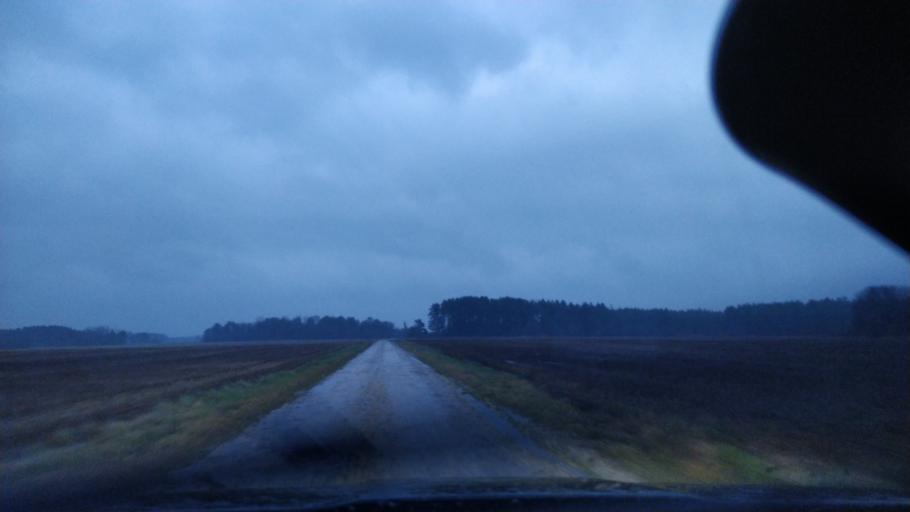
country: EE
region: Laeaene
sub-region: Lihula vald
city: Lihula
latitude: 58.8497
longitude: 23.9890
